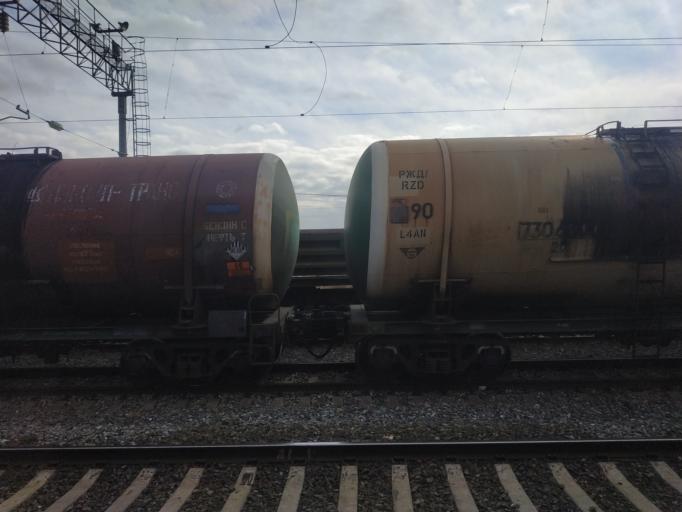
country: RU
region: Volgograd
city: Volgograd
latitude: 48.6703
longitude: 44.4618
